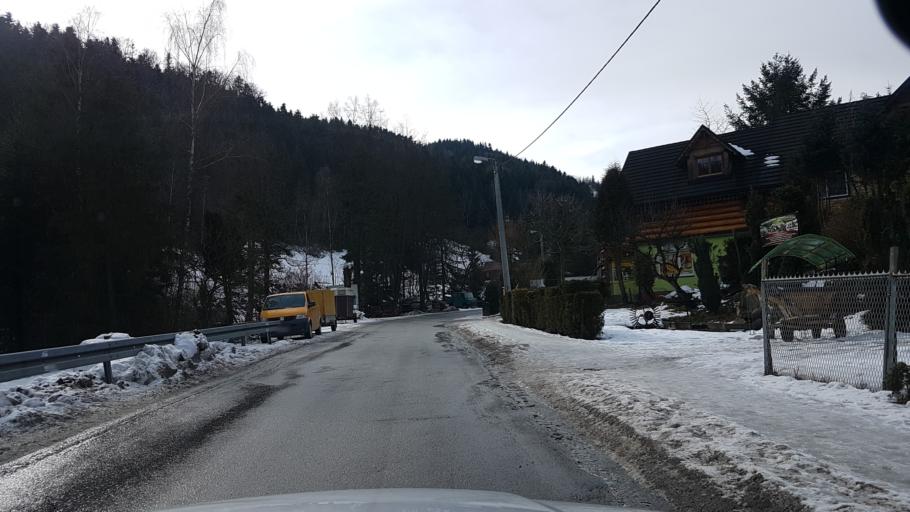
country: PL
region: Lesser Poland Voivodeship
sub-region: Powiat nowosadecki
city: Piwniczna-Zdroj
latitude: 49.4253
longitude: 20.6624
